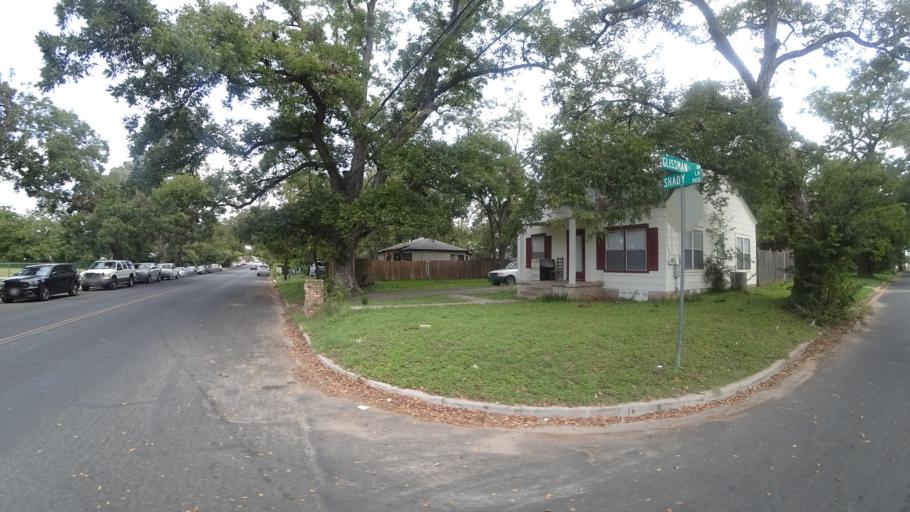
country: US
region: Texas
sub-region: Travis County
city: Austin
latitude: 30.2565
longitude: -97.6955
